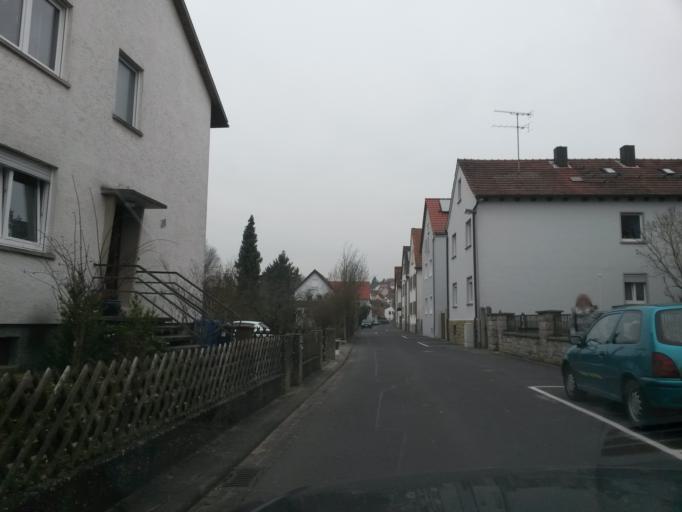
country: DE
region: Bavaria
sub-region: Regierungsbezirk Unterfranken
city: Rimpar
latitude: 49.8549
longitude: 9.9614
